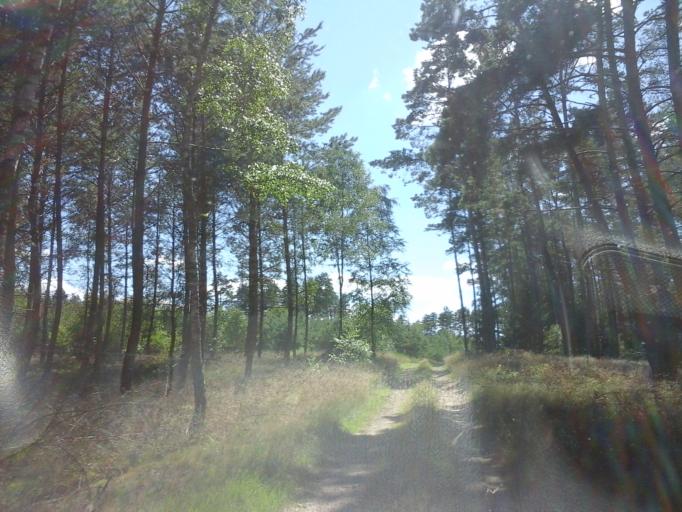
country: PL
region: West Pomeranian Voivodeship
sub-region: Powiat choszczenski
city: Drawno
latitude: 53.2750
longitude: 15.7346
